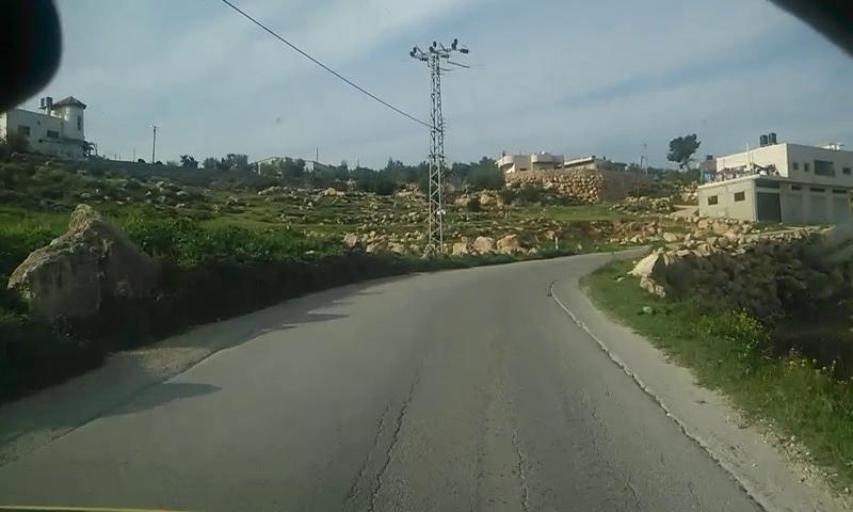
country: PS
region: West Bank
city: Bayt Ula
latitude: 31.5859
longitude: 35.0235
